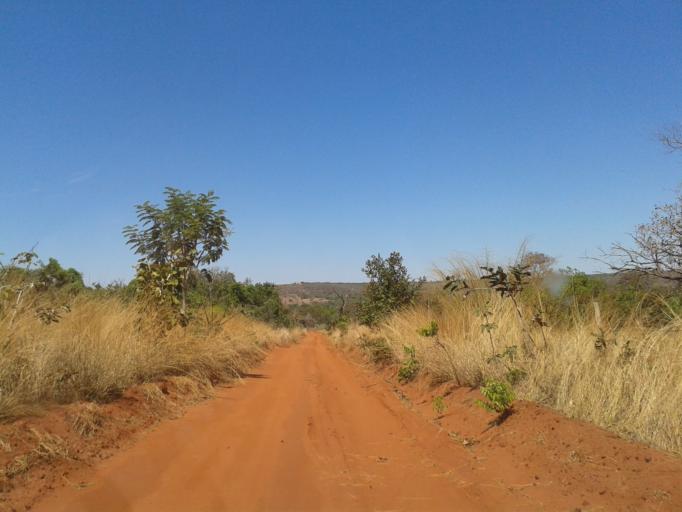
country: BR
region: Minas Gerais
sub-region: Ituiutaba
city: Ituiutaba
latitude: -19.1079
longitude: -49.2714
